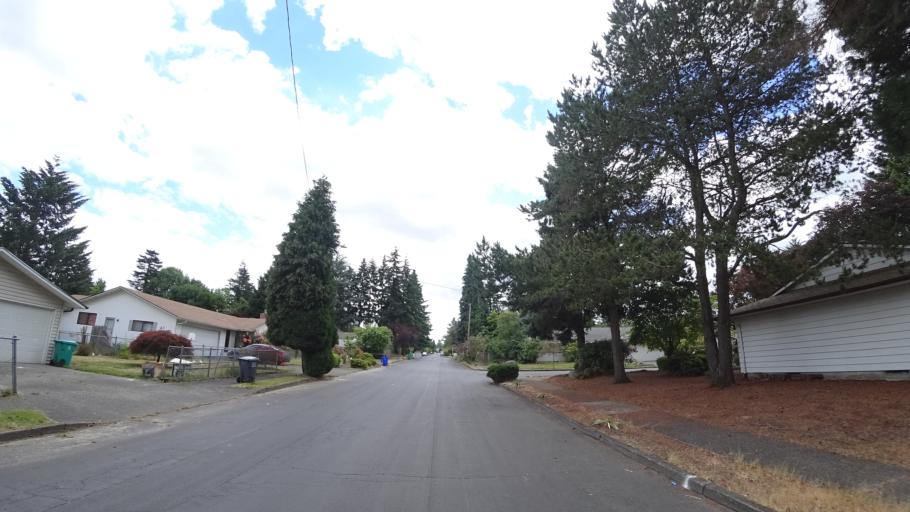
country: US
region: Oregon
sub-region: Multnomah County
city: Portland
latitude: 45.5600
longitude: -122.6070
